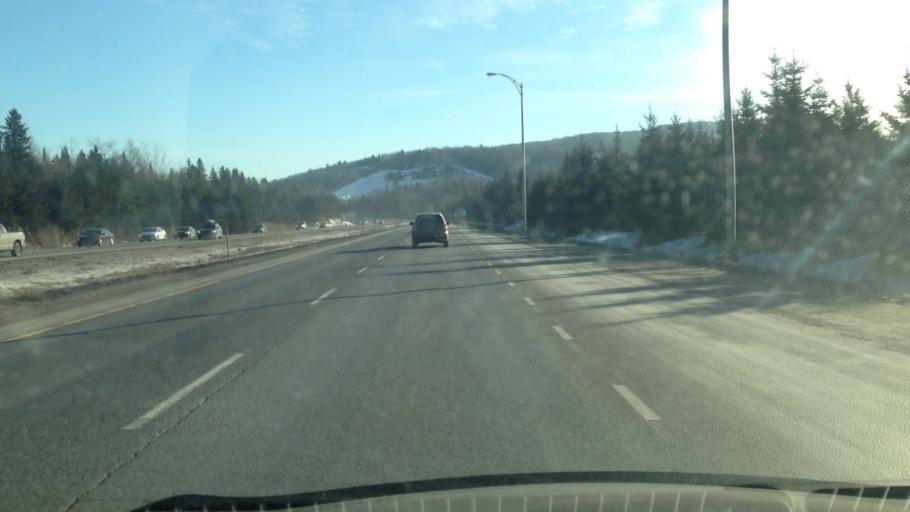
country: CA
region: Quebec
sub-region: Laurentides
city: Saint-Sauveur
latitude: 45.8879
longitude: -74.1370
